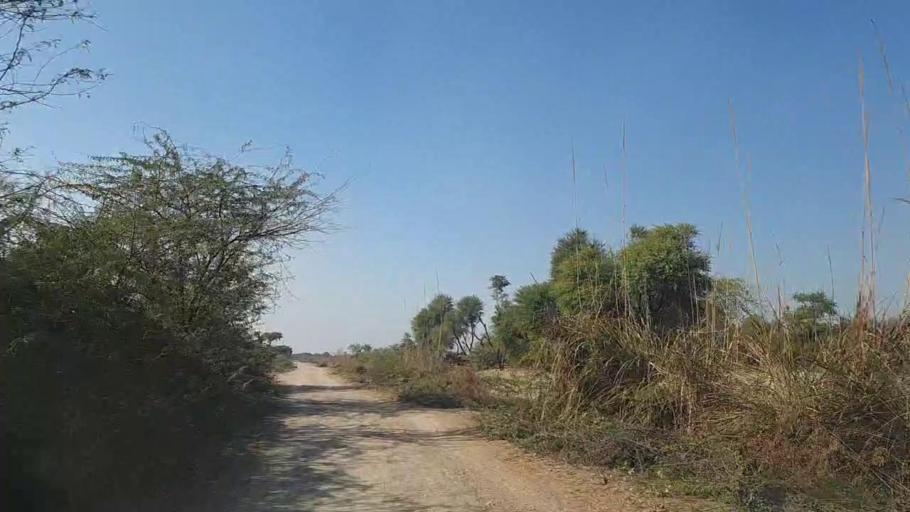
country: PK
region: Sindh
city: Shahpur Chakar
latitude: 26.2109
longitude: 68.6166
